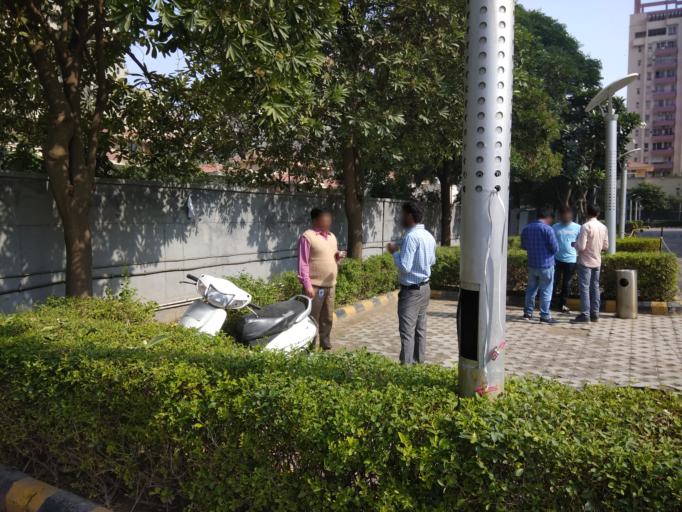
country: IN
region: Haryana
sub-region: Gurgaon
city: Gurgaon
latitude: 28.4134
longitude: 77.0436
